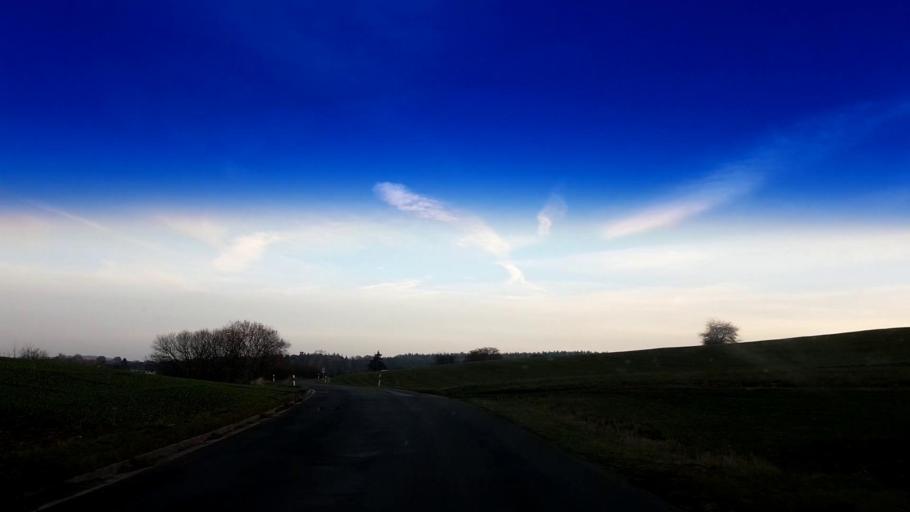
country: DE
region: Bavaria
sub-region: Upper Franconia
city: Stegaurach
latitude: 49.8625
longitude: 10.8207
